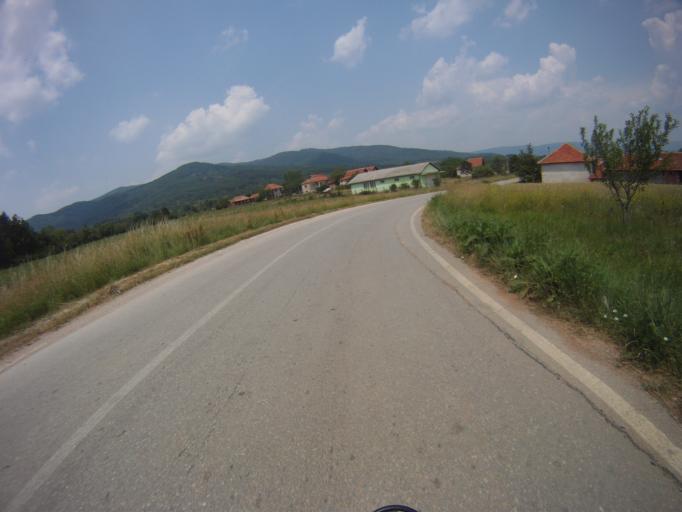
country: RS
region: Central Serbia
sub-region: Nisavski Okrug
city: Gadzin Han
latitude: 43.2062
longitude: 21.9845
